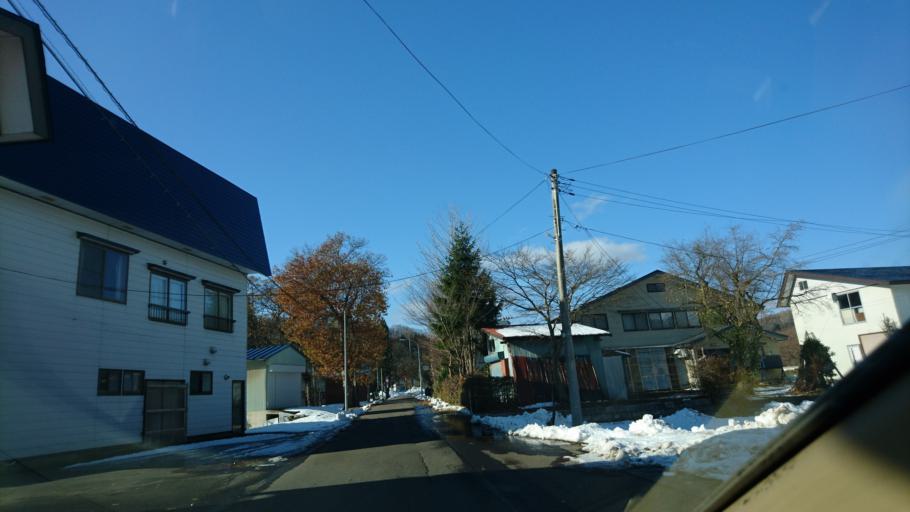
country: JP
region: Akita
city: Yokotemachi
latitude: 39.3099
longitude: 140.7625
